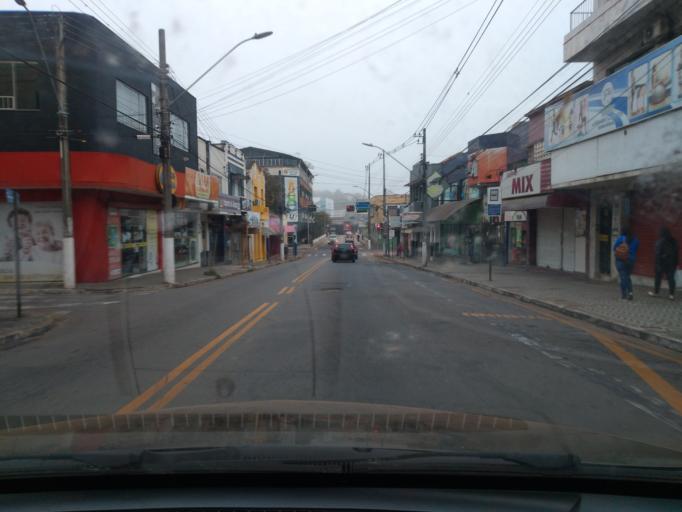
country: BR
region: Minas Gerais
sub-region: Tres Coracoes
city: Tres Coracoes
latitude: -21.6990
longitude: -45.2578
